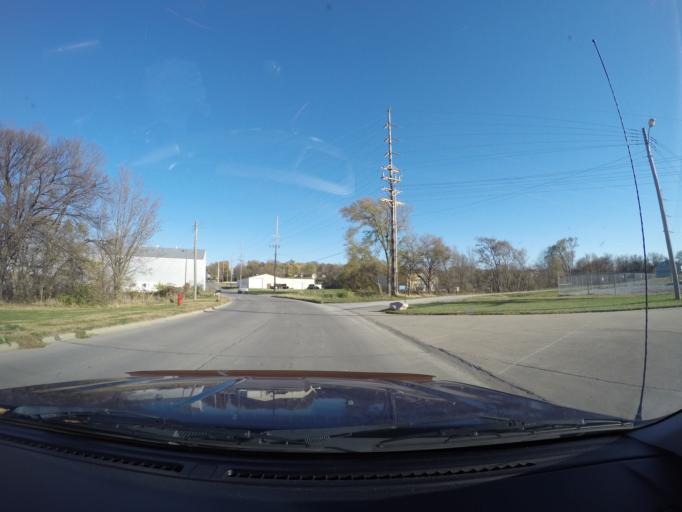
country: US
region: Nebraska
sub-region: Otoe County
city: Nebraska City
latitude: 40.6663
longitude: -95.8678
